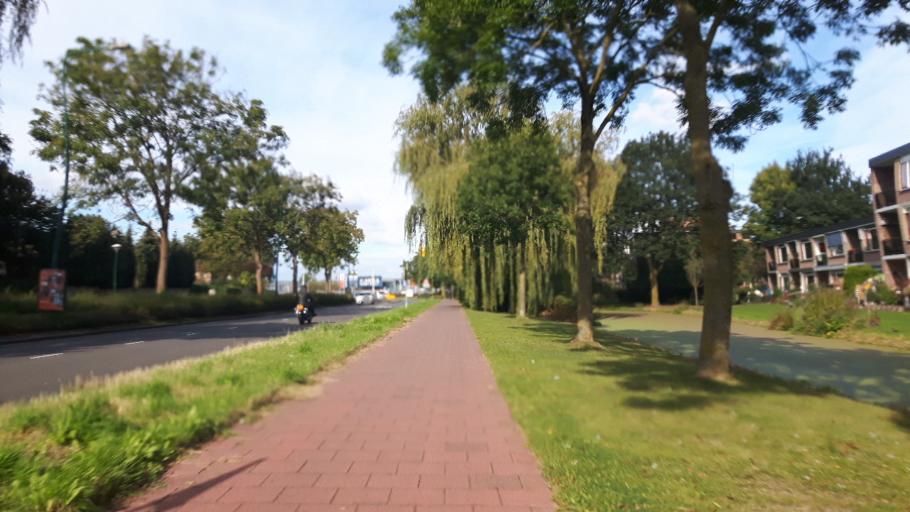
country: NL
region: Utrecht
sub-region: Gemeente Woerden
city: Woerden
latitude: 52.0803
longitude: 4.8706
